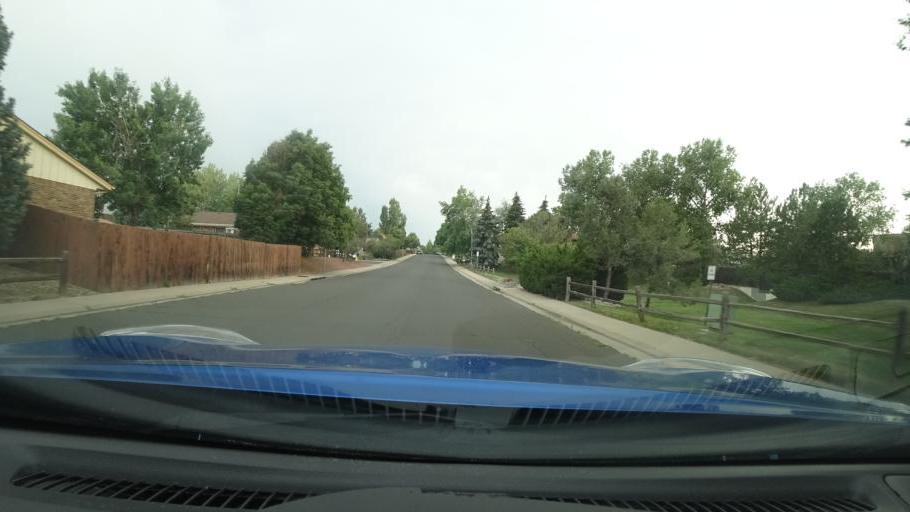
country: US
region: Colorado
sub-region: Adams County
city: Aurora
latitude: 39.6911
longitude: -104.8255
